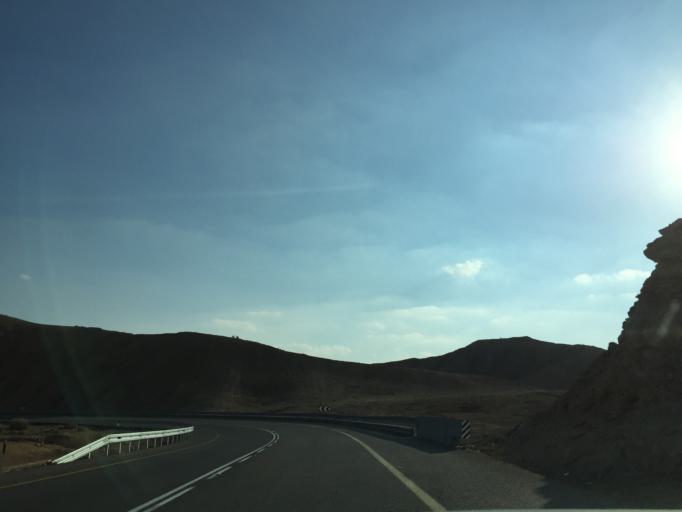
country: IL
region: Southern District
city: `En Boqeq
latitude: 31.1830
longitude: 35.2905
